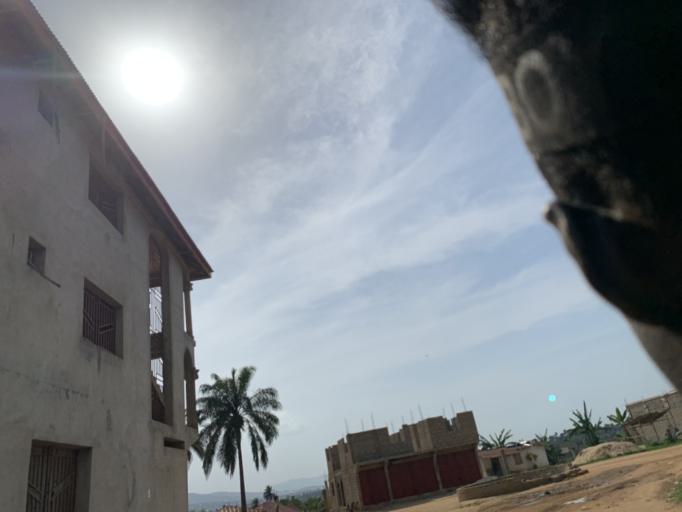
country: SL
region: Western Area
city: Waterloo
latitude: 8.3465
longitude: -13.0516
